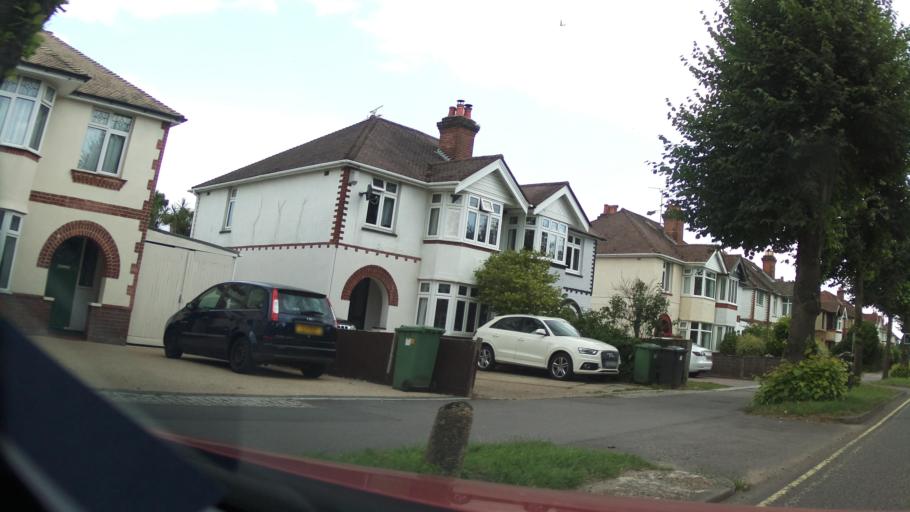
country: GB
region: England
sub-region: Hampshire
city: Eastleigh
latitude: 50.9713
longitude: -1.3661
